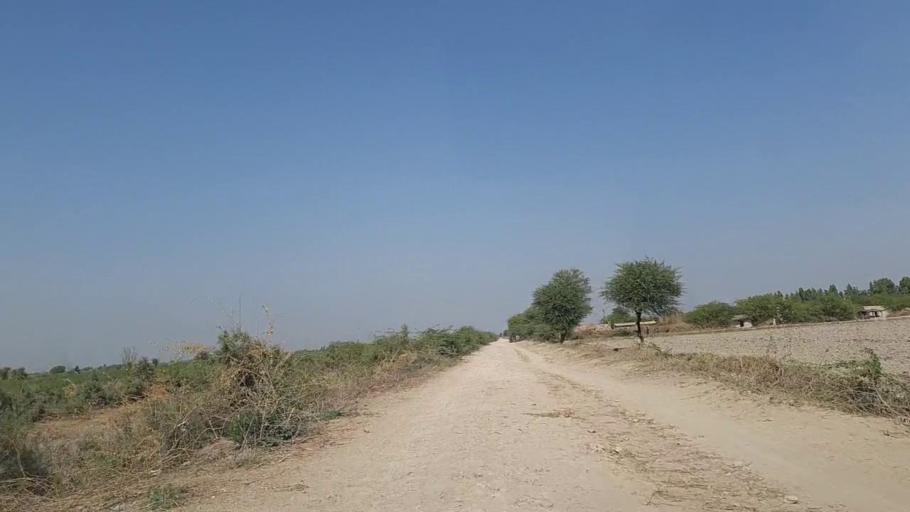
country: PK
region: Sindh
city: Samaro
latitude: 25.2020
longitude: 69.4041
